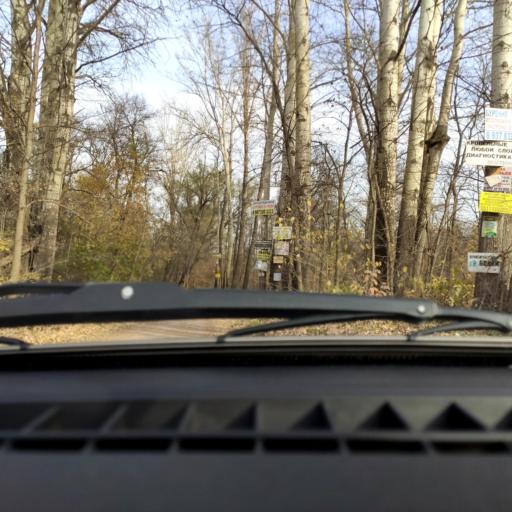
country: RU
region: Bashkortostan
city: Ufa
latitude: 54.7822
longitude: 56.1797
